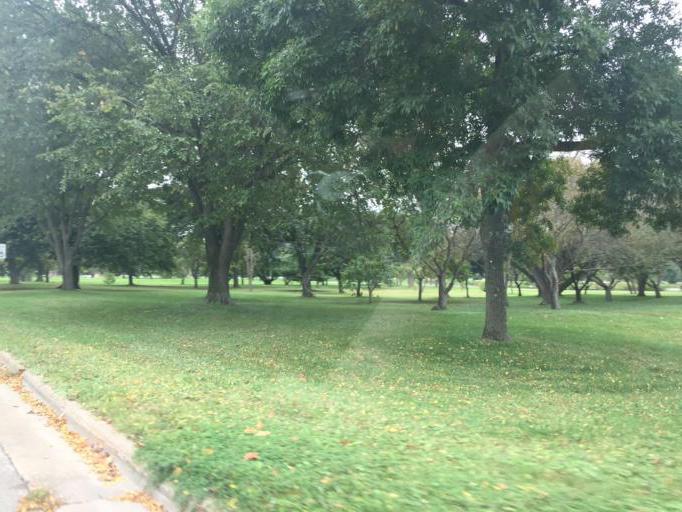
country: US
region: Minnesota
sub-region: Winona County
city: Winona
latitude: 44.0390
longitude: -91.6283
